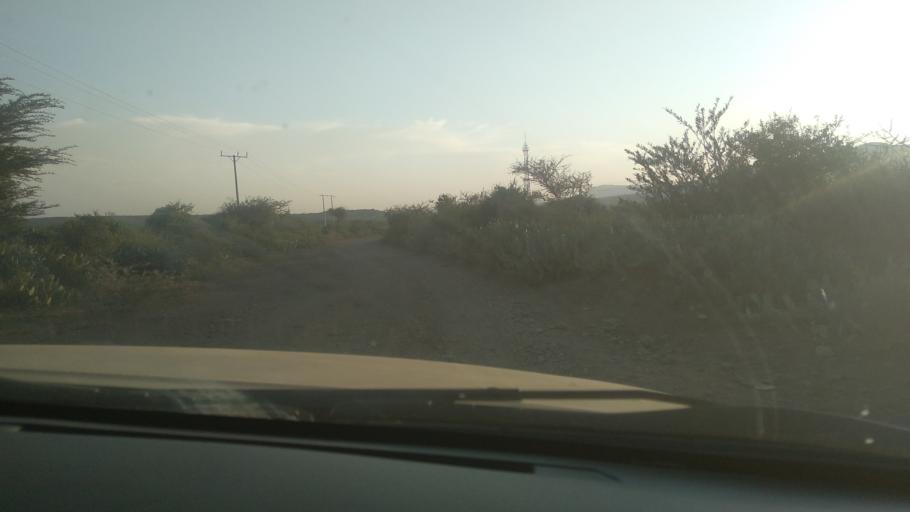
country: ET
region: Oromiya
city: Asbe Teferi
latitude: 9.2629
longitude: 40.7993
